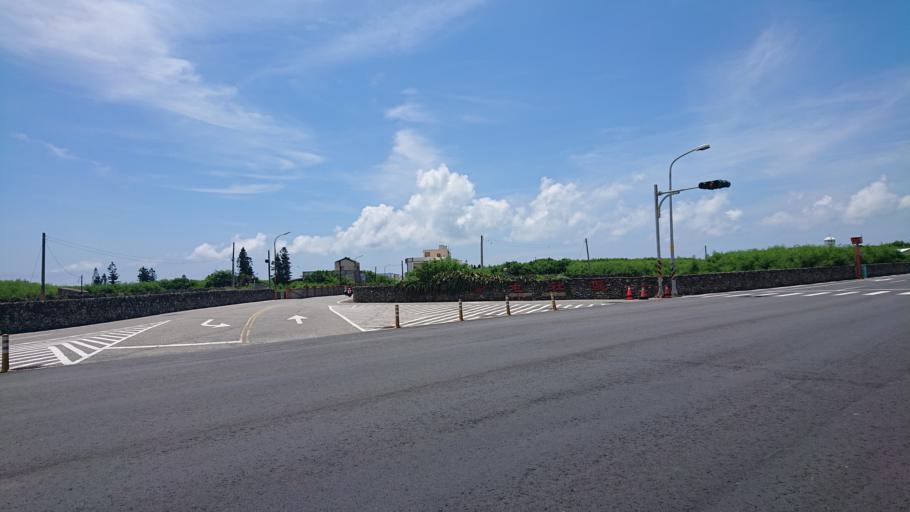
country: TW
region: Taiwan
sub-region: Penghu
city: Ma-kung
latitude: 23.6116
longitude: 119.6092
